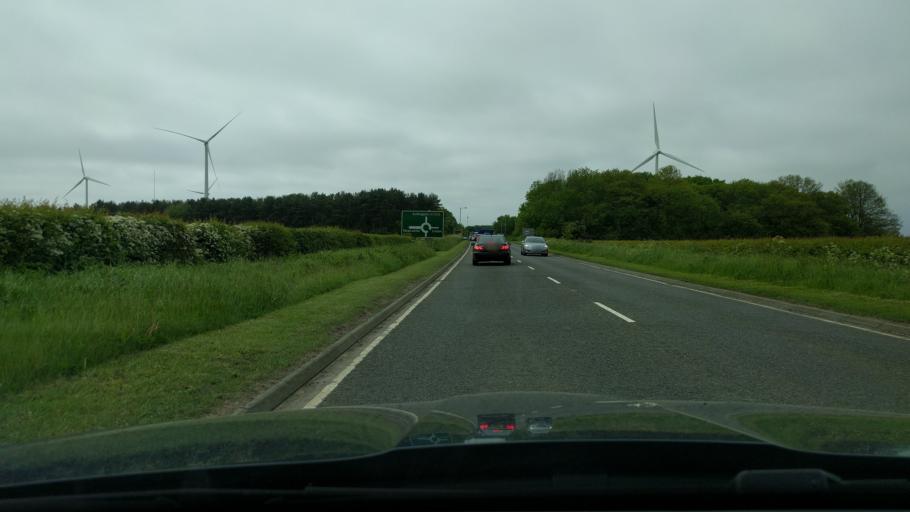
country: GB
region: England
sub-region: Northumberland
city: Cresswell
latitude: 55.2106
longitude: -1.5720
